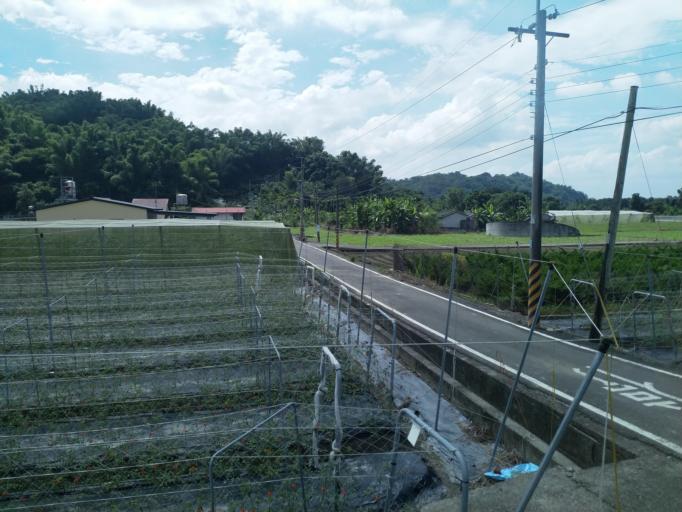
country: TW
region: Taiwan
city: Yujing
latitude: 22.9125
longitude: 120.5744
